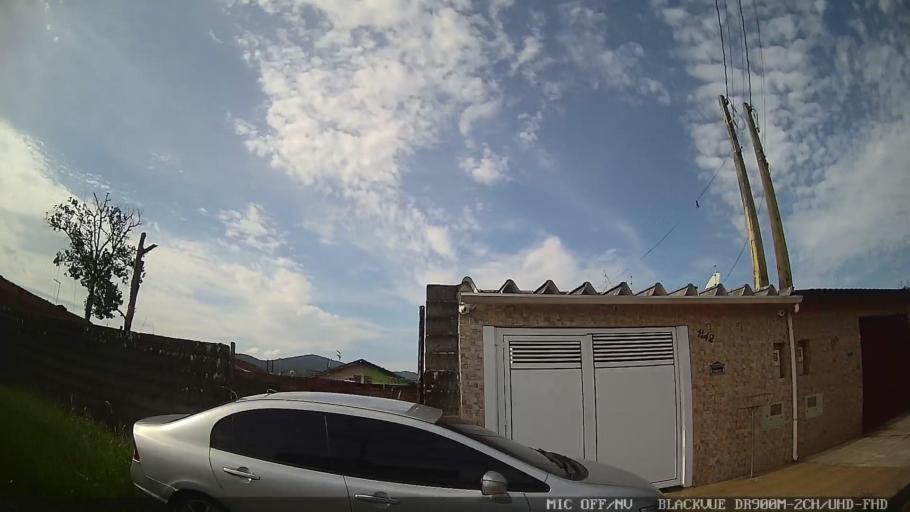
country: BR
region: Sao Paulo
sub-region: Itanhaem
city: Itanhaem
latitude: -24.1595
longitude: -46.7699
